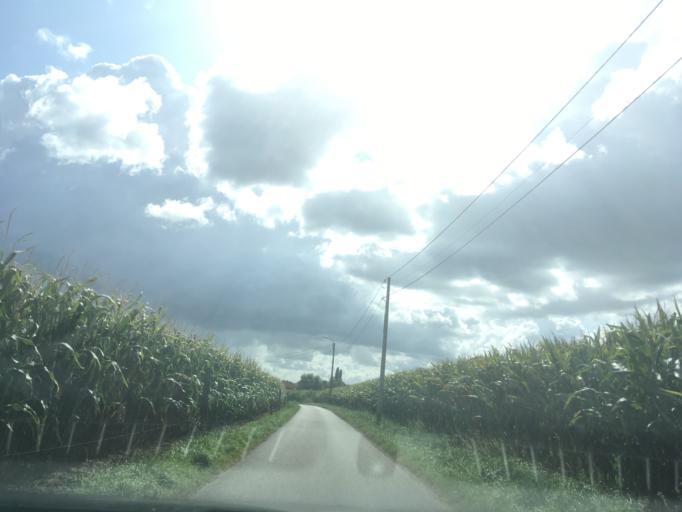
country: BE
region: Flanders
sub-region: Provincie West-Vlaanderen
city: Kortemark
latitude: 51.0185
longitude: 3.0508
